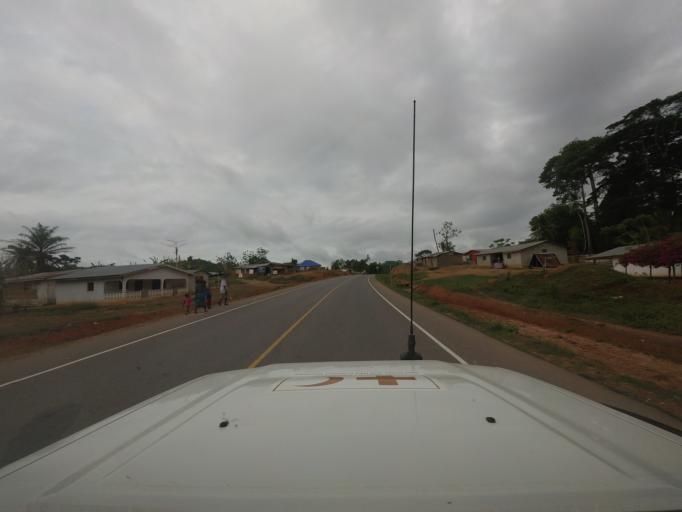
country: LR
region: Bong
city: Gbarnga
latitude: 7.0050
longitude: -9.3954
